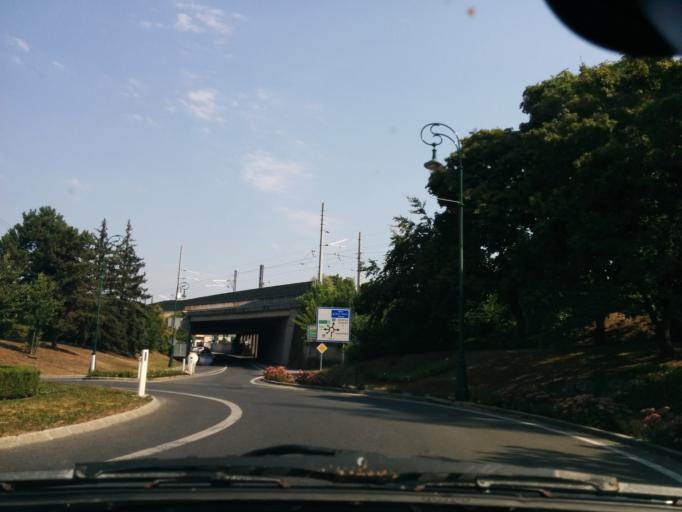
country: AT
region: Lower Austria
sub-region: Politischer Bezirk Tulln
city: Tulln
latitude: 48.3299
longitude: 16.0590
